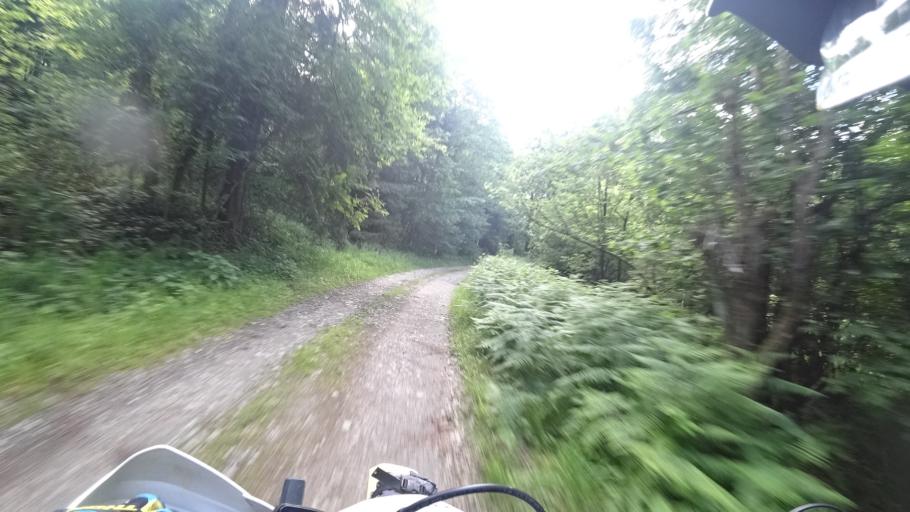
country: SI
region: Osilnica
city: Osilnica
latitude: 45.4634
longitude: 14.7090
